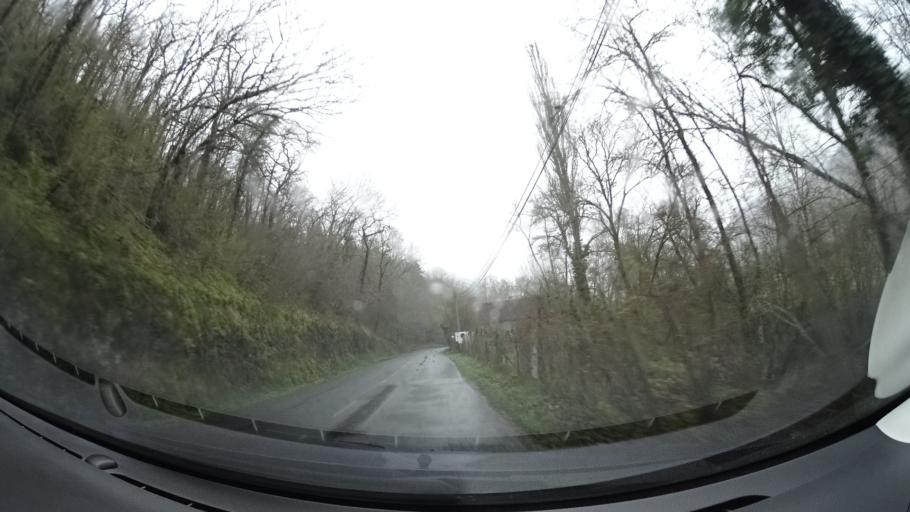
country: FR
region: Aquitaine
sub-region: Departement de la Dordogne
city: Cenac-et-Saint-Julien
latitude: 44.8017
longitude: 1.1597
